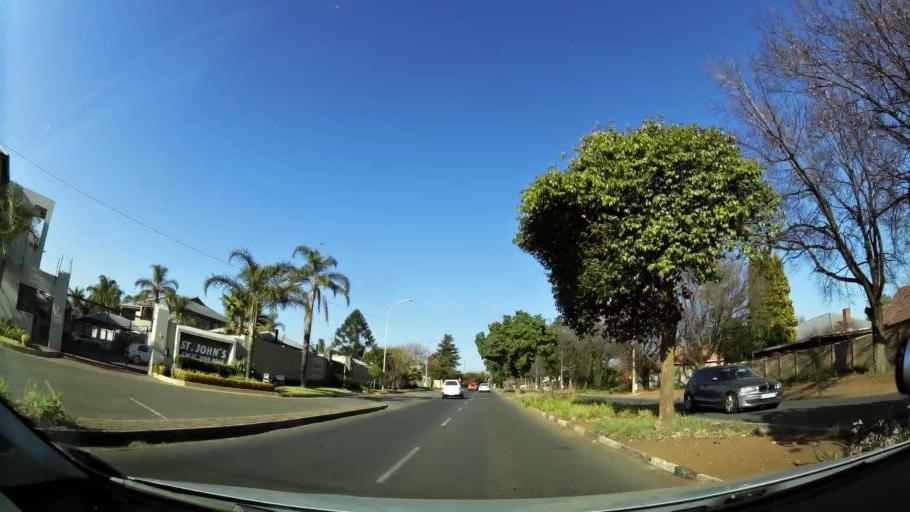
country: ZA
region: Gauteng
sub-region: City of Johannesburg Metropolitan Municipality
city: Modderfontein
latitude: -26.1507
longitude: 28.1629
